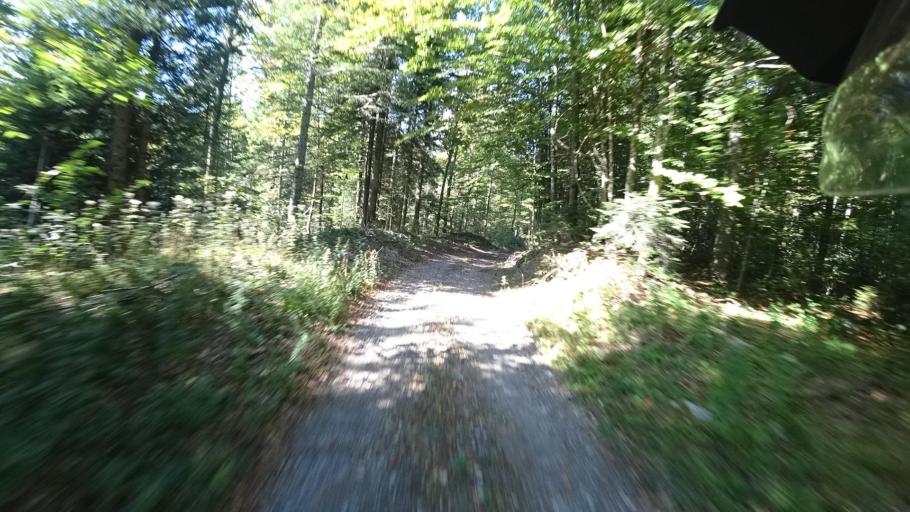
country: HR
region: Primorsko-Goranska
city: Vrbovsko
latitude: 45.2665
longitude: 15.1084
